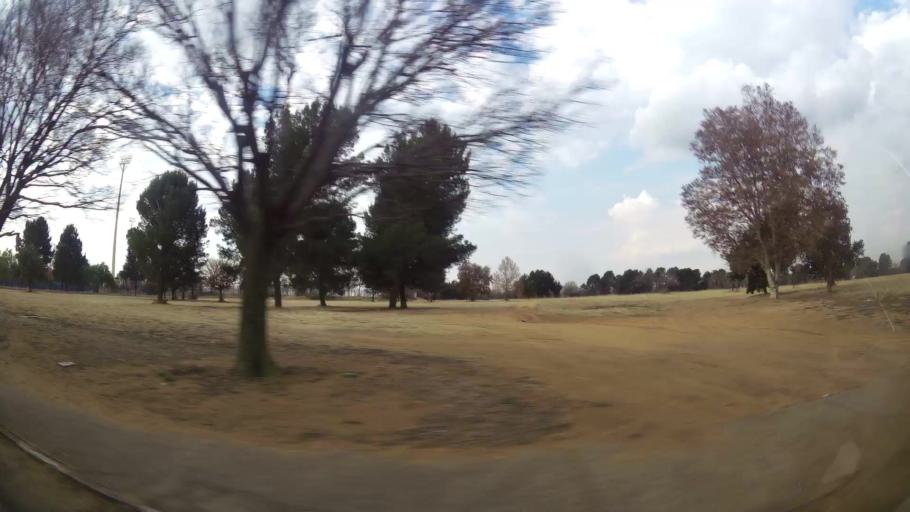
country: ZA
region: Orange Free State
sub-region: Fezile Dabi District Municipality
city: Sasolburg
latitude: -26.7970
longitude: 27.8260
